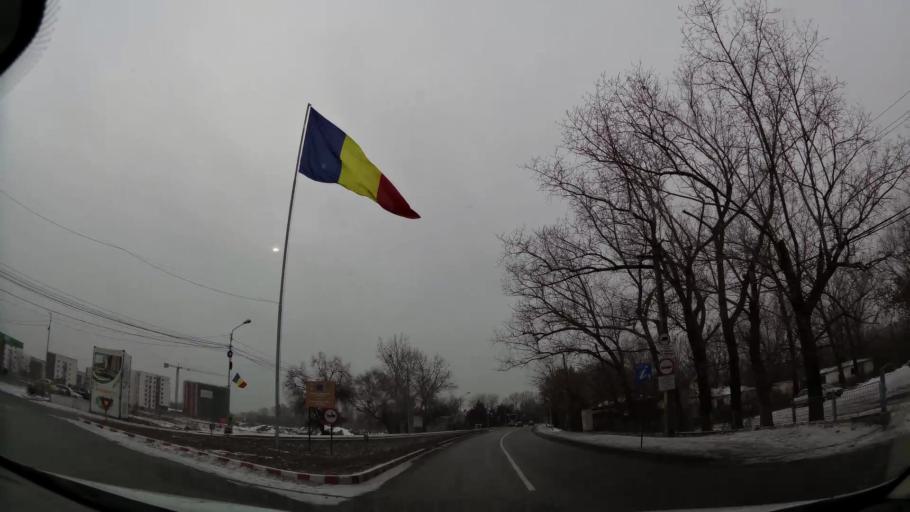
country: RO
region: Dambovita
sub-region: Municipiul Targoviste
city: Targoviste
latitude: 44.9412
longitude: 25.4577
